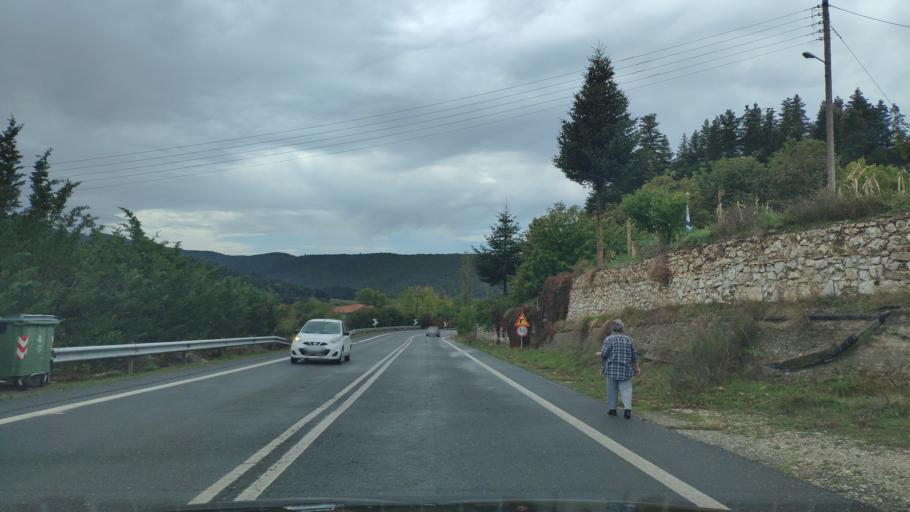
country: GR
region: Peloponnese
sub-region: Nomos Arkadias
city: Dimitsana
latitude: 37.6366
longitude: 22.0899
